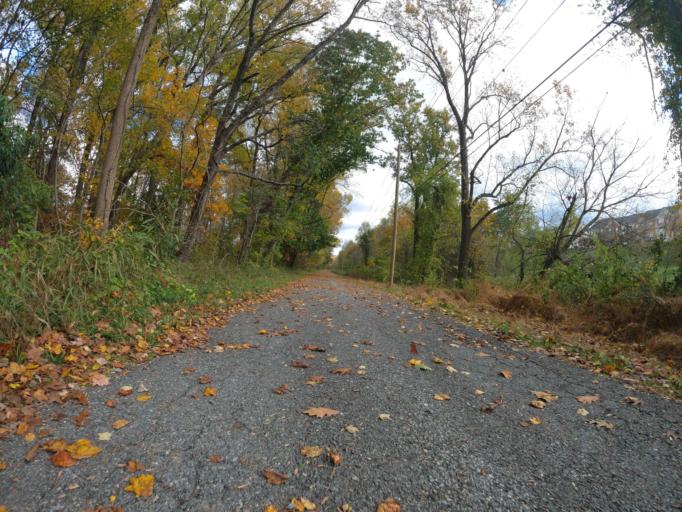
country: US
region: Maryland
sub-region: Carroll County
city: Mount Airy
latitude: 39.3698
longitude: -77.1343
